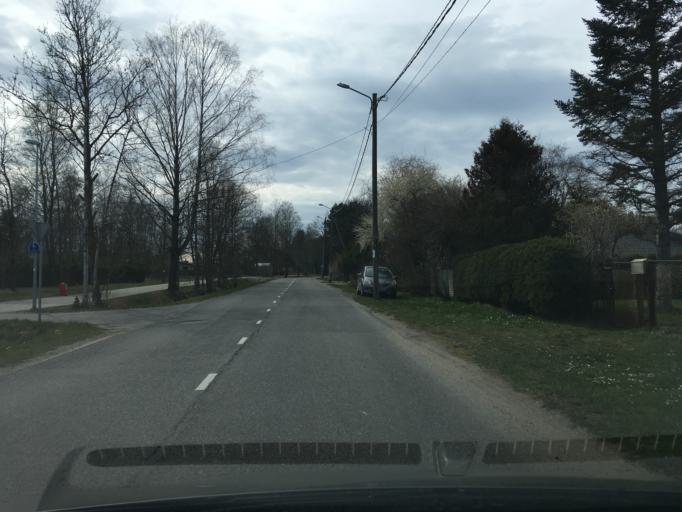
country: EE
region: Harju
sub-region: Joelaehtme vald
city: Loo
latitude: 59.4739
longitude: 24.9463
